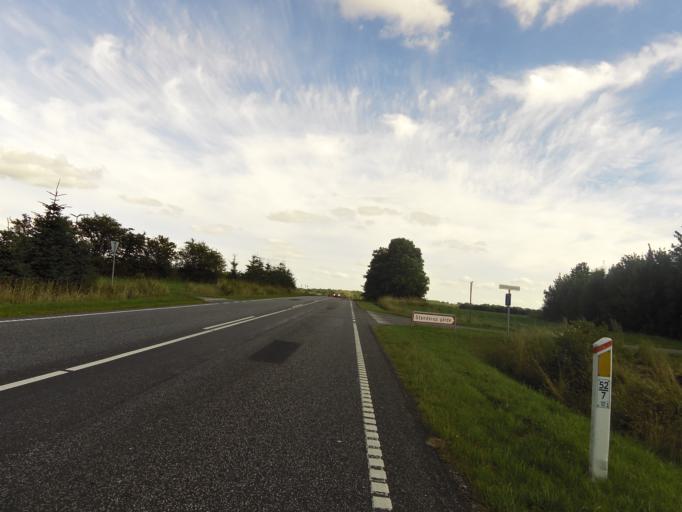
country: DK
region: South Denmark
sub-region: Tonder Kommune
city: Toftlund
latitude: 55.2087
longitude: 9.0451
